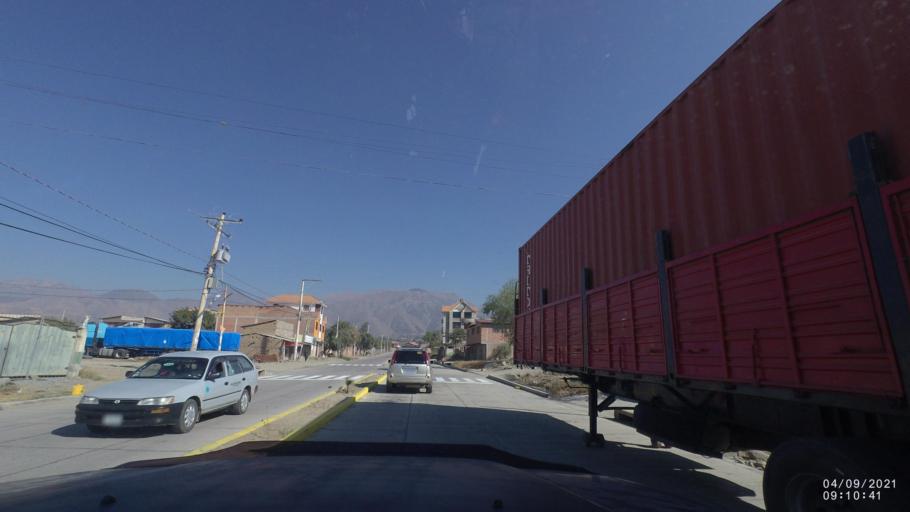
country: BO
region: Cochabamba
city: Sipe Sipe
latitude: -17.3916
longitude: -66.3323
